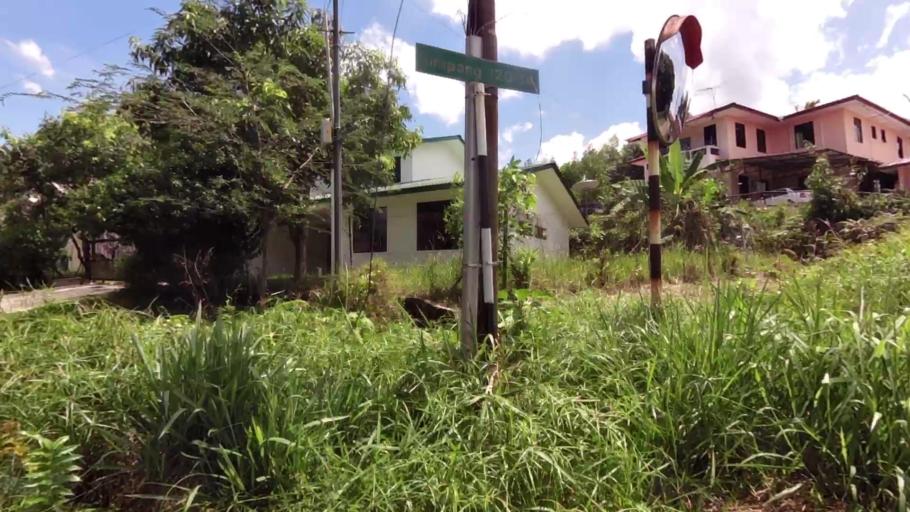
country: BN
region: Brunei and Muara
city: Bandar Seri Begawan
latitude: 4.9397
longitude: 114.9679
